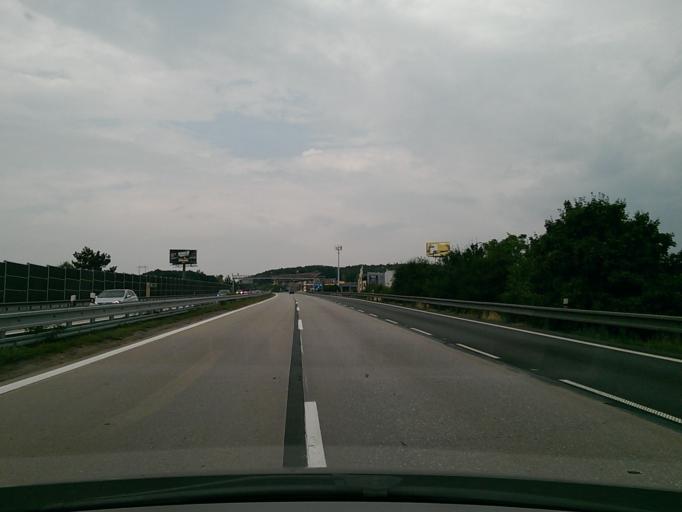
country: CZ
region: South Moravian
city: Troubsko
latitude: 49.1805
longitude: 16.4852
